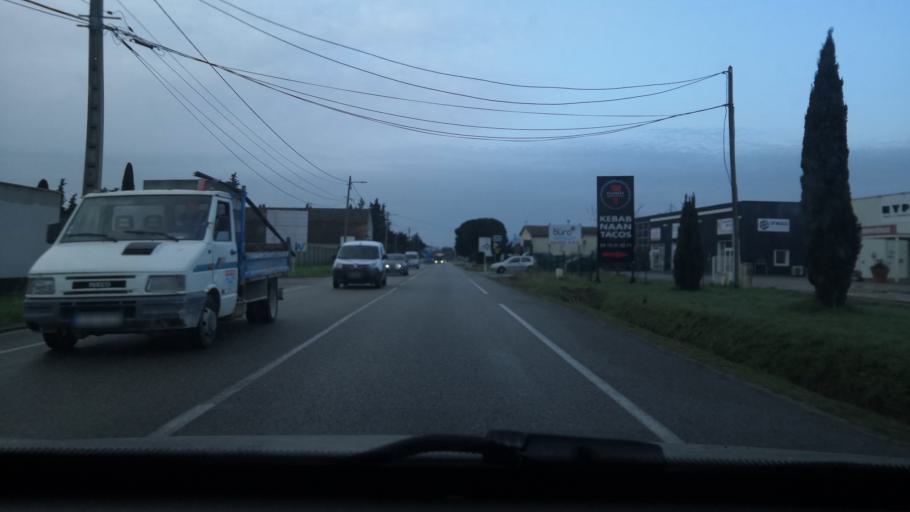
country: FR
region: Rhone-Alpes
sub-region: Departement de la Drome
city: Montelimar
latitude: 44.5308
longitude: 4.7365
